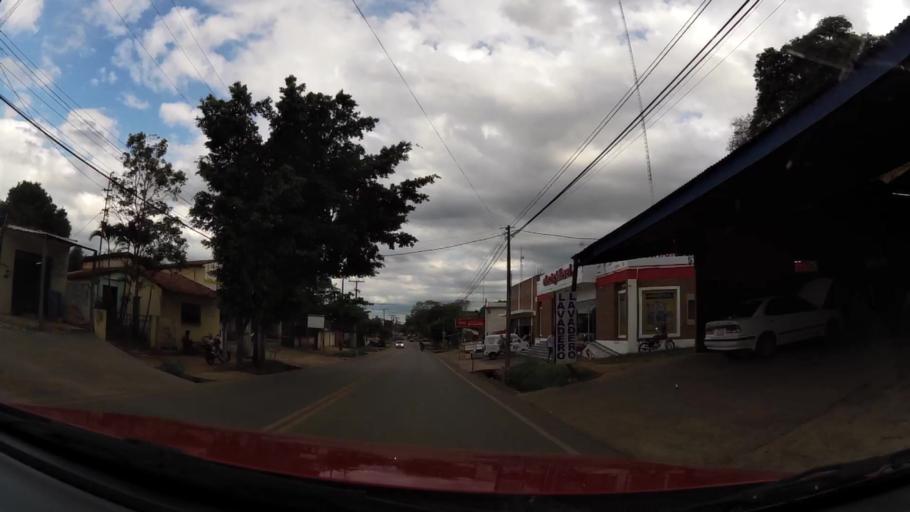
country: PY
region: Central
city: San Lorenzo
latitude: -25.2807
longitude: -57.4844
